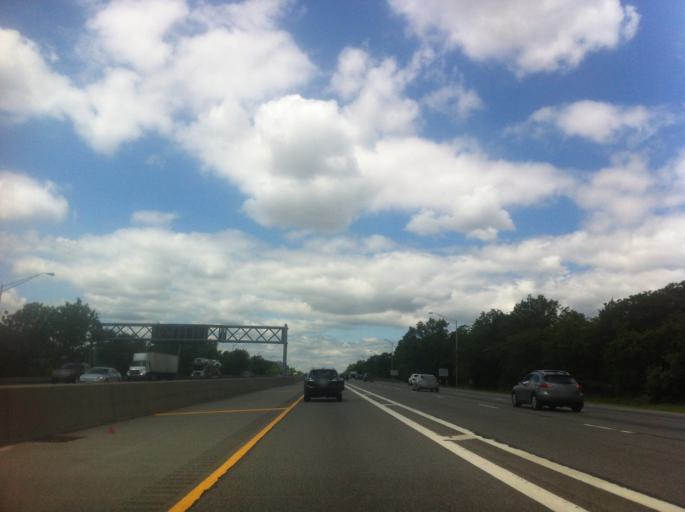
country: US
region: New York
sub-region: Suffolk County
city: Islandia
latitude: 40.8090
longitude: -73.1798
